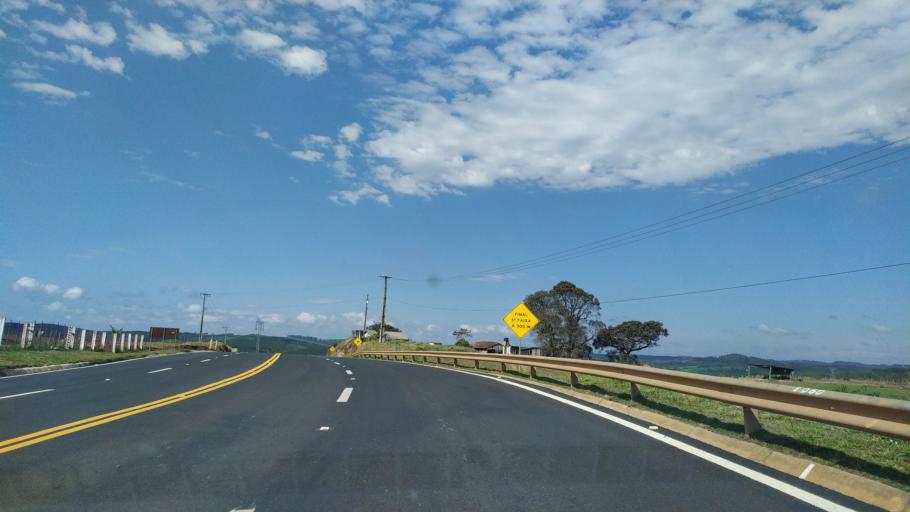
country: BR
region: Parana
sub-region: Telemaco Borba
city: Telemaco Borba
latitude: -24.2814
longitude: -50.7140
